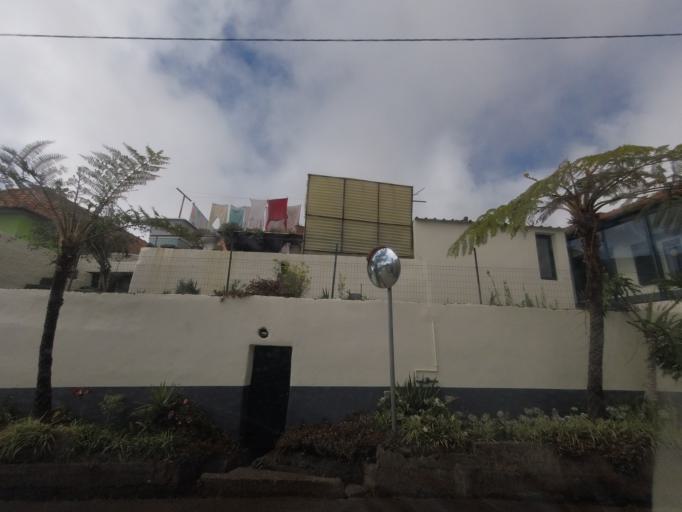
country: PT
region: Madeira
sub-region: Calheta
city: Faja da Ovelha
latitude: 32.7635
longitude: -17.2197
